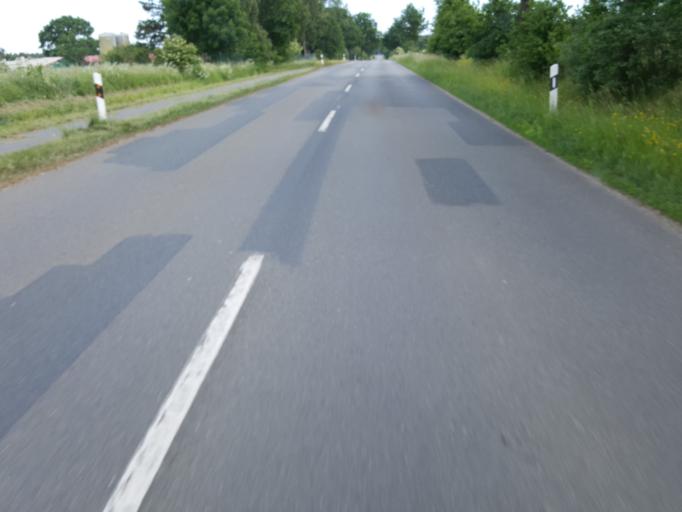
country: DE
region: Lower Saxony
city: Husum
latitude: 52.5999
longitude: 9.2472
